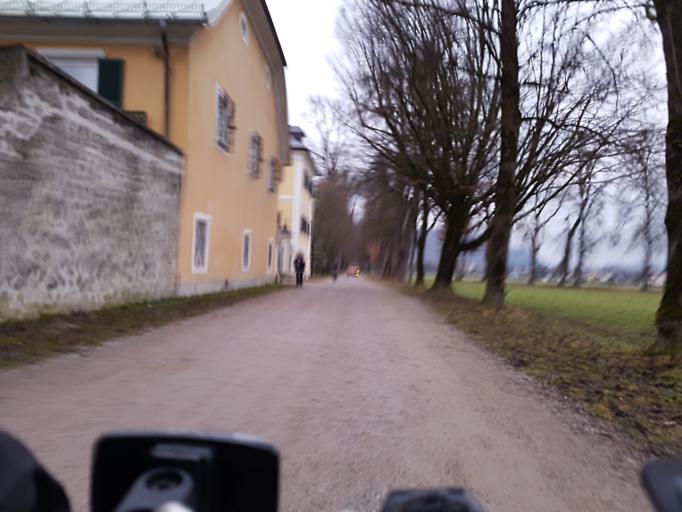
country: AT
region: Salzburg
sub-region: Salzburg Stadt
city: Salzburg
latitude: 47.7790
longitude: 13.0598
